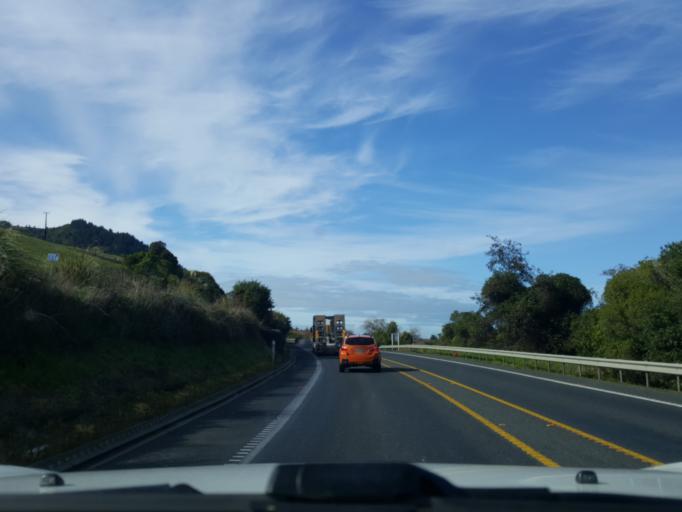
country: NZ
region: Waikato
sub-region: Waikato District
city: Ngaruawahia
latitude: -37.5998
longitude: 175.1654
